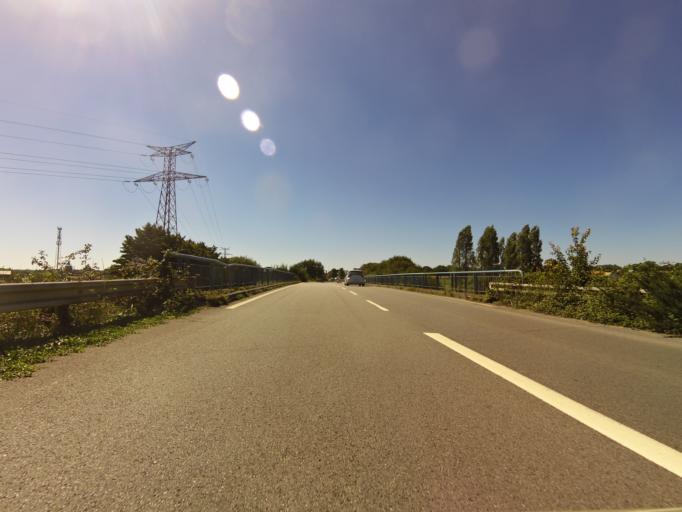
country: FR
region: Brittany
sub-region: Departement du Morbihan
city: Lanester
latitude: 47.7807
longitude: -3.3445
